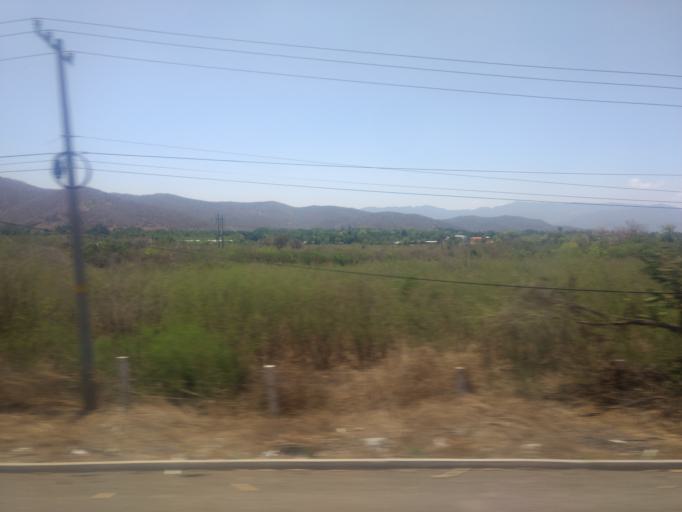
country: MX
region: Colima
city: Coquimatlan
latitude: 19.1408
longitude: -103.7711
